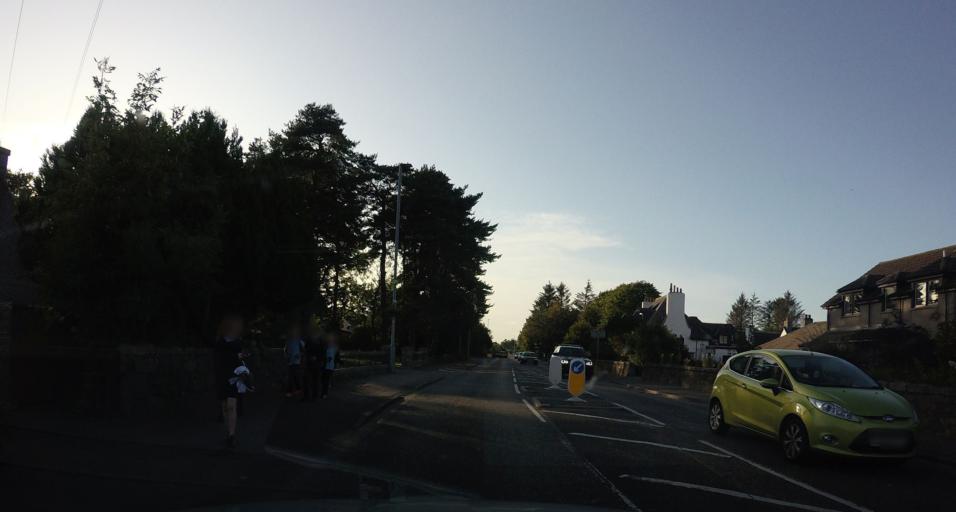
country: GB
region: Scotland
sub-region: Aberdeenshire
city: Westhill
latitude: 57.1502
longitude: -2.2998
